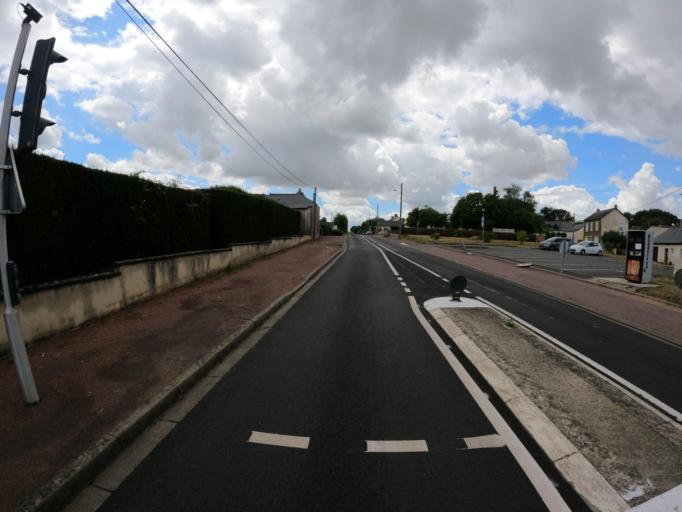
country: FR
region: Pays de la Loire
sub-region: Departement de la Sarthe
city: Sable-sur-Sarthe
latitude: 47.8263
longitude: -0.3889
